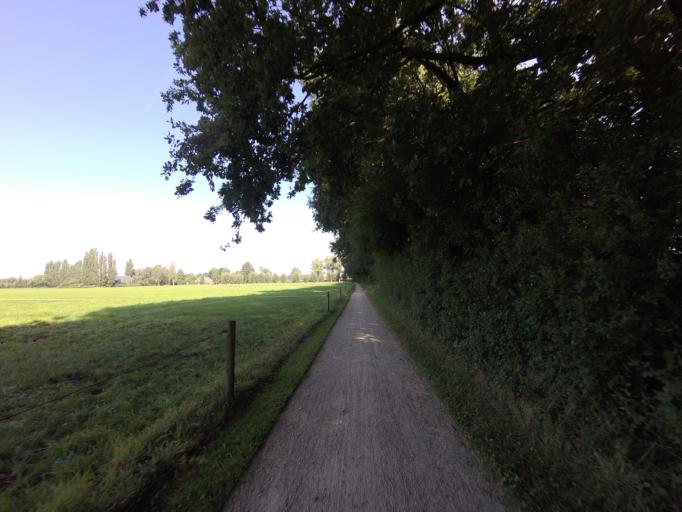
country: NL
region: Gelderland
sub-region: Oost Gelre
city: Lichtenvoorde
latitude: 52.0108
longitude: 6.5203
